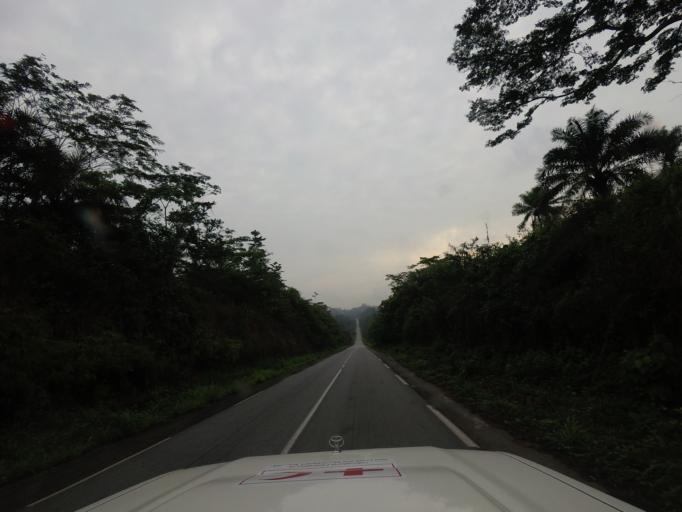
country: LR
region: Lofa
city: Voinjama
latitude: 8.6177
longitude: -9.7521
